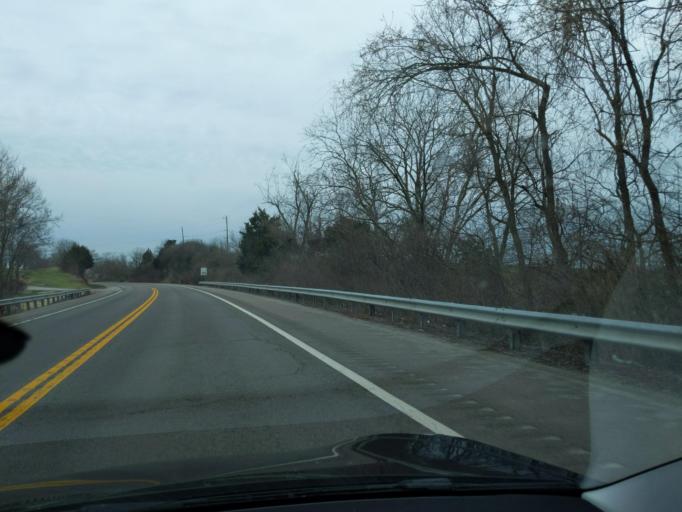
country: US
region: Kentucky
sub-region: Madison County
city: Richmond
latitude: 37.8810
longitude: -84.2957
